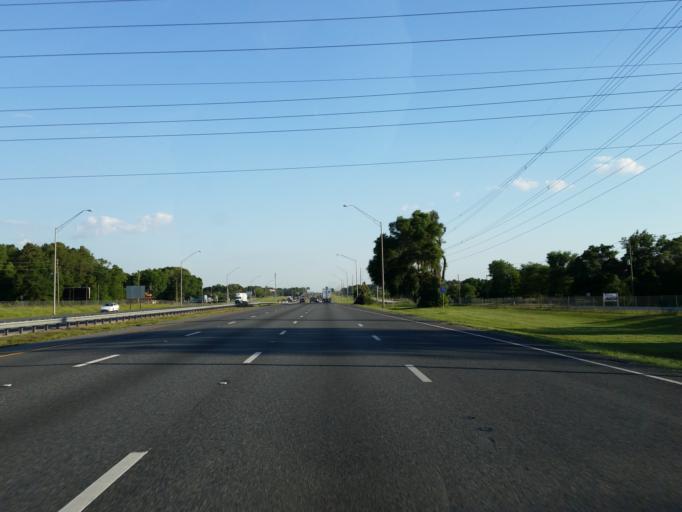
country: US
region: Florida
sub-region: Marion County
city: Ocala
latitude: 29.1807
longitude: -82.1850
